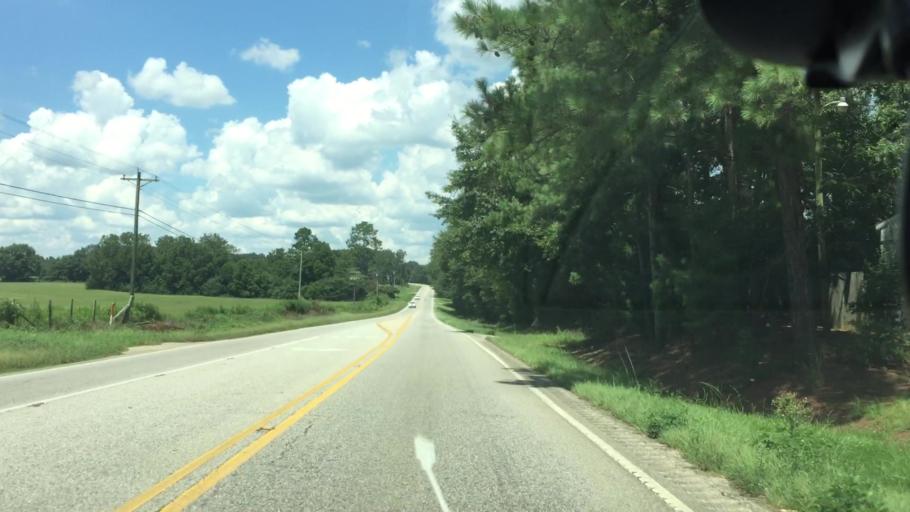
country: US
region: Alabama
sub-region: Pike County
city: Troy
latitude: 31.7314
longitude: -85.9576
